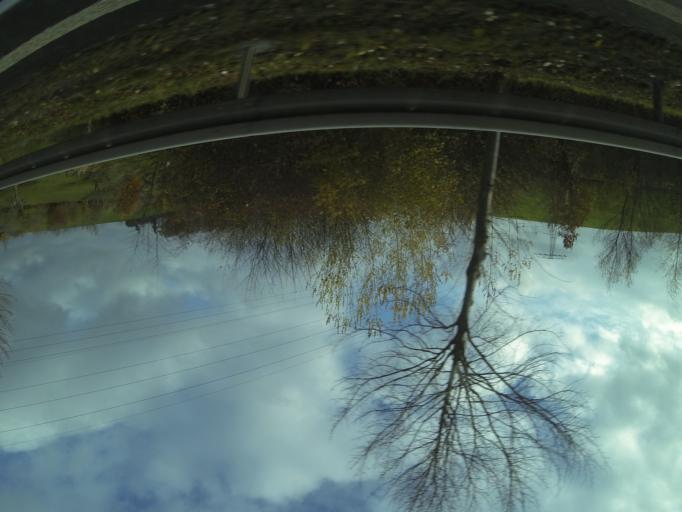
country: DE
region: Thuringia
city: Altenburg
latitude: 50.9599
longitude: 12.4307
